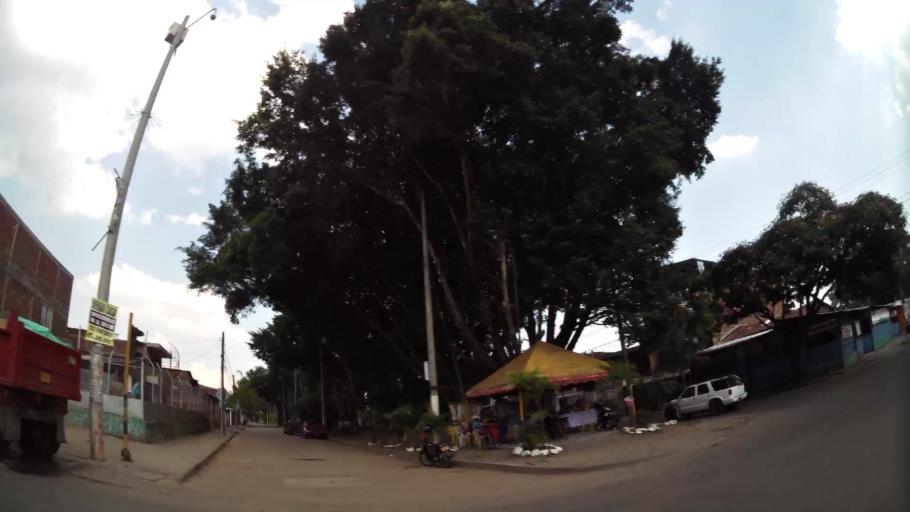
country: CO
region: Valle del Cauca
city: Cali
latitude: 3.4147
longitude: -76.5177
